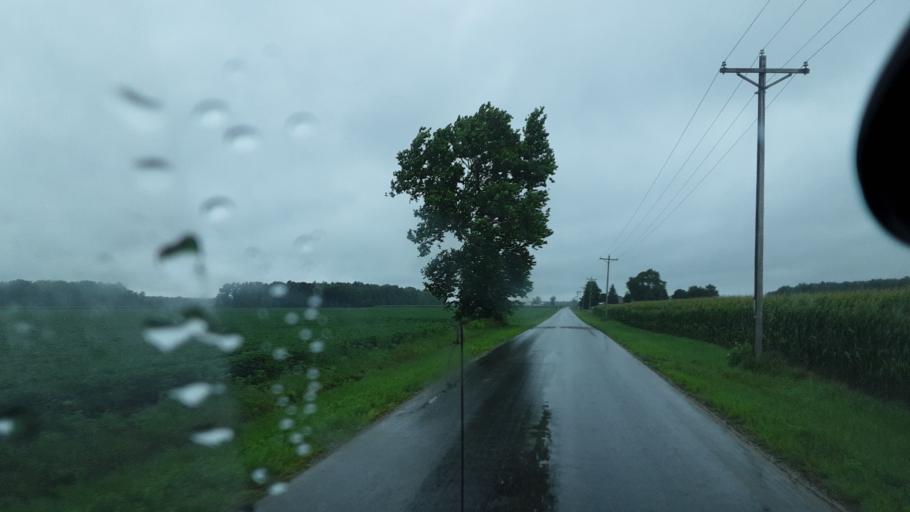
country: US
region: Indiana
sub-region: Adams County
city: Decatur
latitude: 40.7478
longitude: -84.8562
